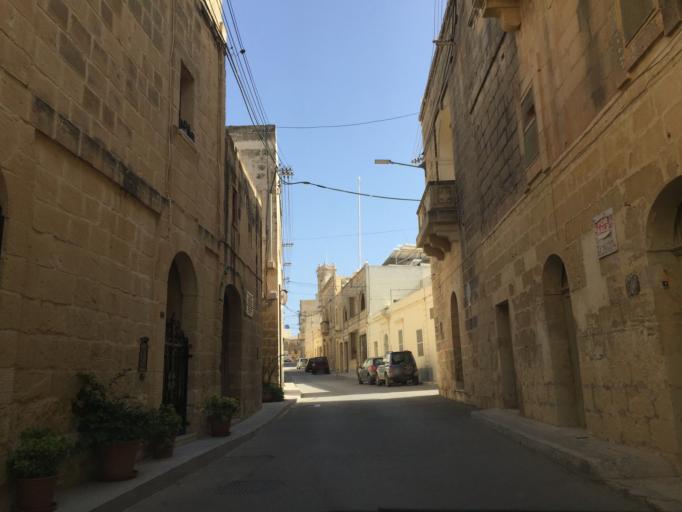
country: MT
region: L-Gharb
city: Gharb
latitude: 36.0617
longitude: 14.2089
